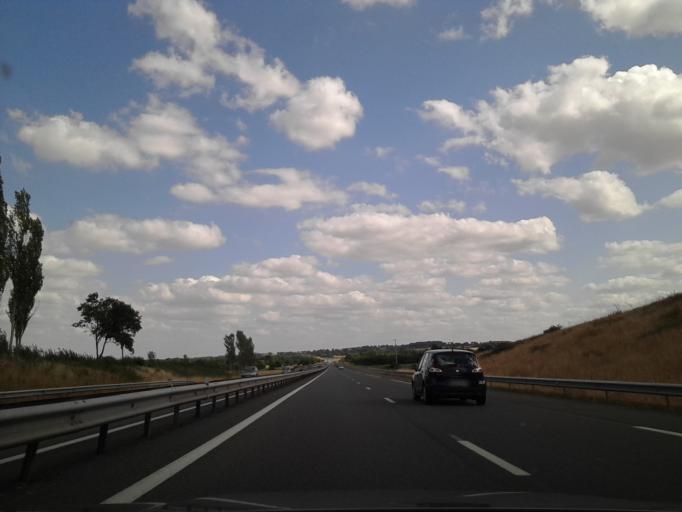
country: FR
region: Auvergne
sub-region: Departement de l'Allier
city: Vallon-en-Sully
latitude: 46.5530
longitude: 2.5485
